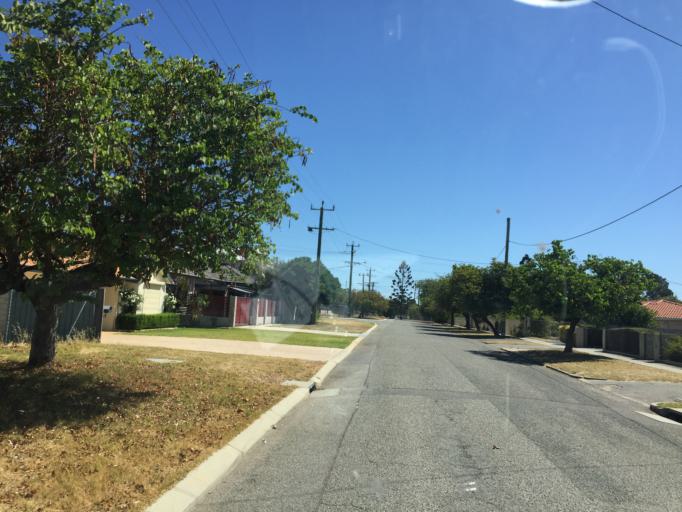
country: AU
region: Western Australia
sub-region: Victoria Park
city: Victoria Park
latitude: -31.9813
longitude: 115.9139
